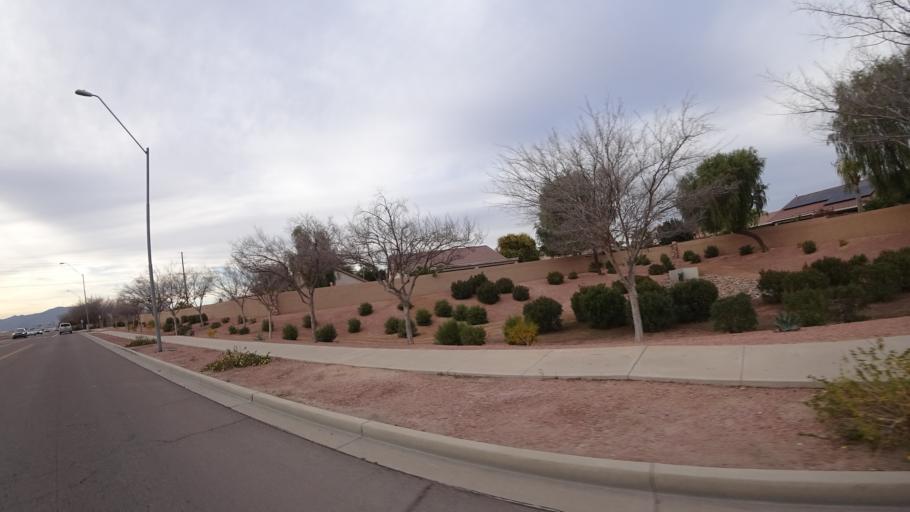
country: US
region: Arizona
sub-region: Maricopa County
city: Surprise
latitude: 33.6243
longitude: -112.4082
